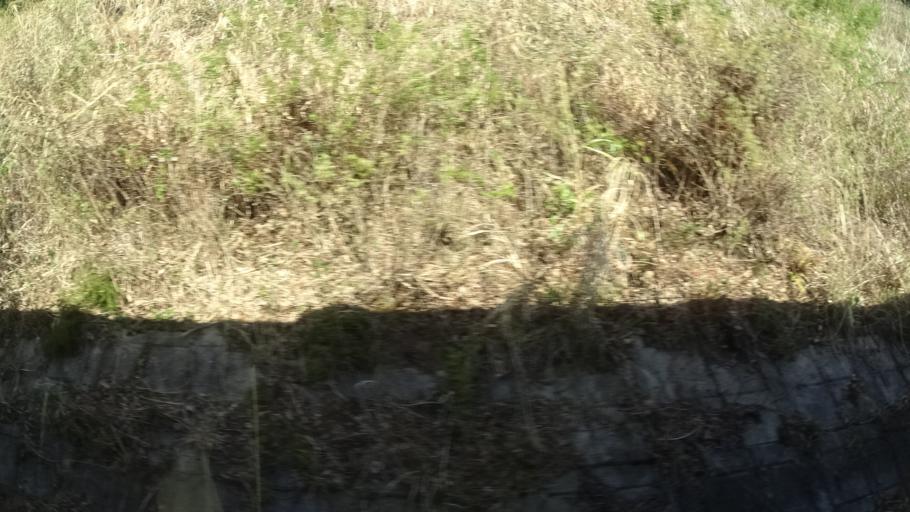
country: JP
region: Fukushima
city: Namie
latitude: 37.5853
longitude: 141.0018
